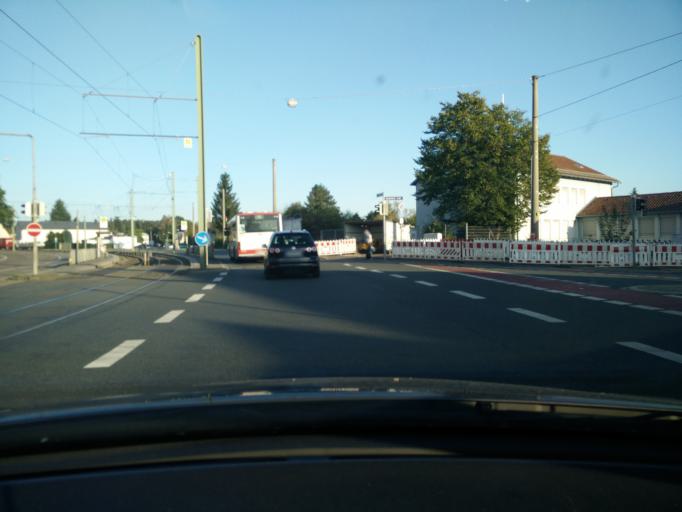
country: DE
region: Bavaria
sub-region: Regierungsbezirk Mittelfranken
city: Nuernberg
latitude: 49.4060
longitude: 11.0873
